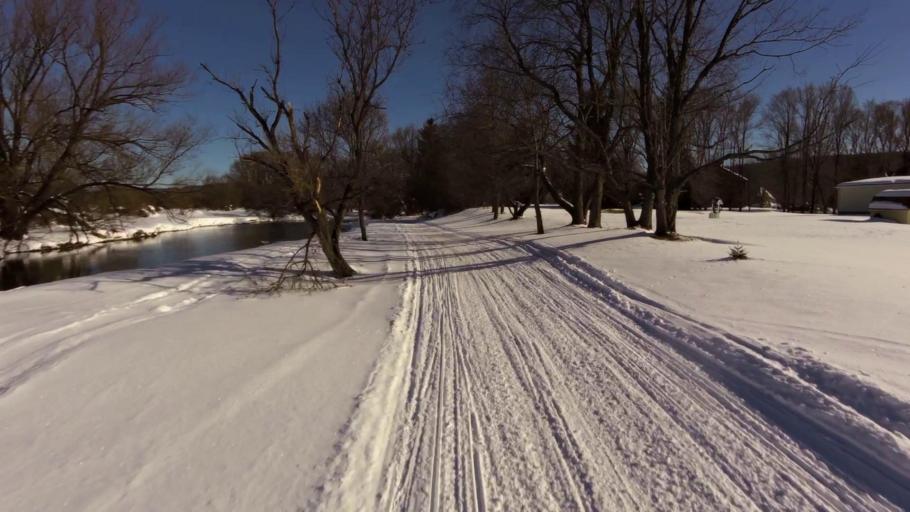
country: US
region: New York
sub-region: Cattaraugus County
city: Franklinville
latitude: 42.3520
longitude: -78.4542
